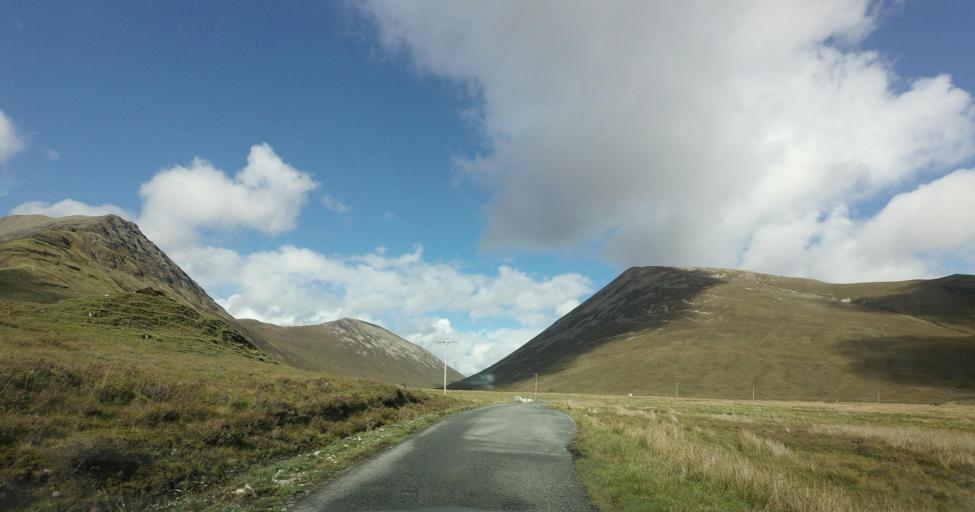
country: GB
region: Scotland
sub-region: Highland
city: Portree
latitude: 57.2264
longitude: -6.0421
